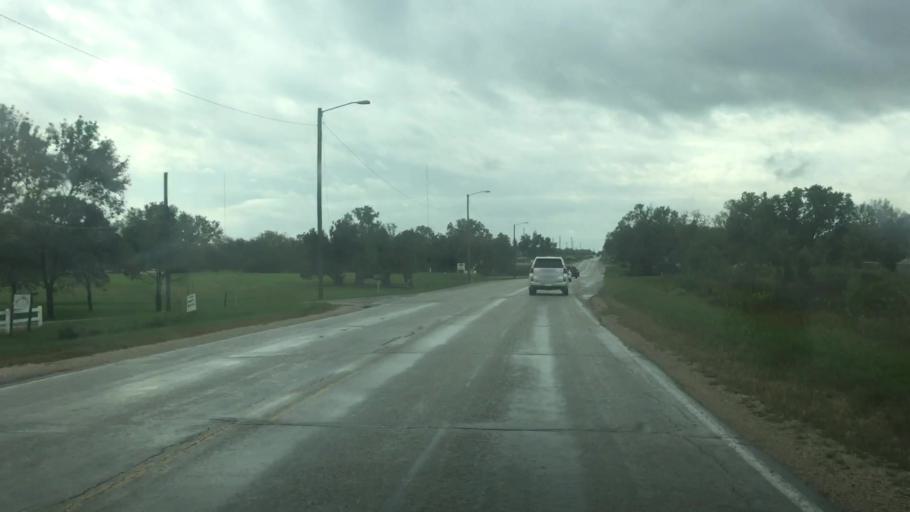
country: US
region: Kansas
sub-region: Allen County
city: Iola
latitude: 37.9022
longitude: -95.4094
